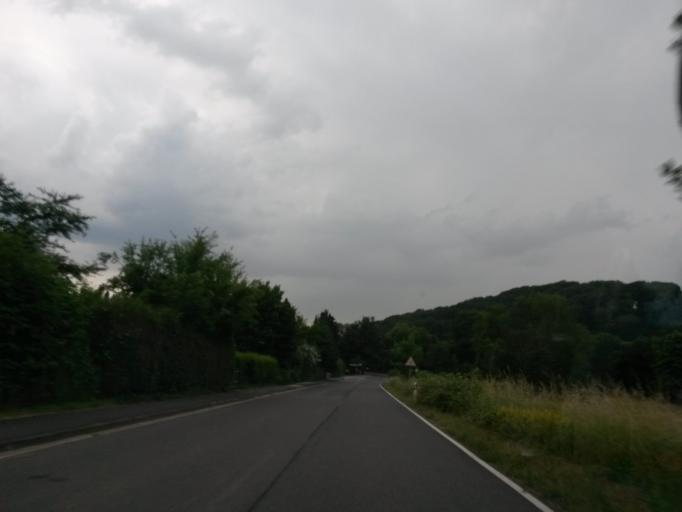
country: DE
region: North Rhine-Westphalia
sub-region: Regierungsbezirk Koln
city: Overath
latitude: 50.9016
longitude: 7.2733
